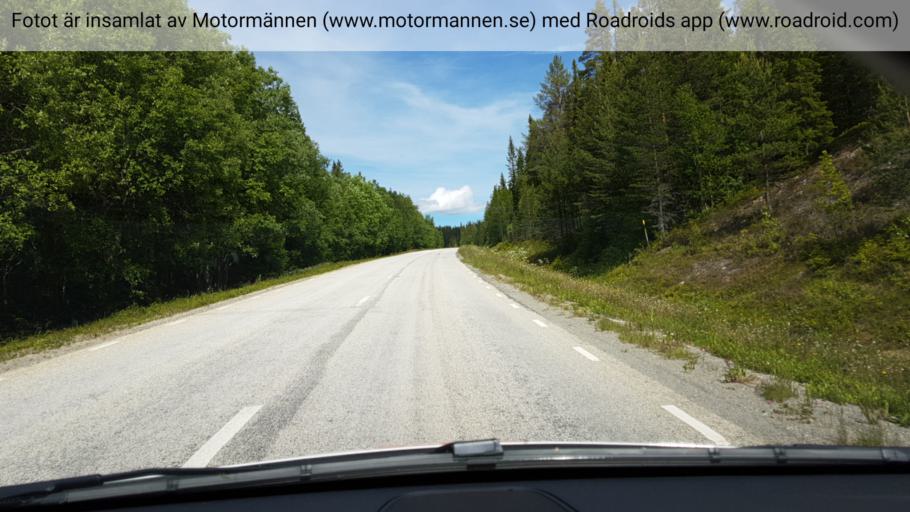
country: SE
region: Jaemtland
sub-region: Bergs Kommun
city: Hoverberg
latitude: 62.5356
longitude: 14.2120
